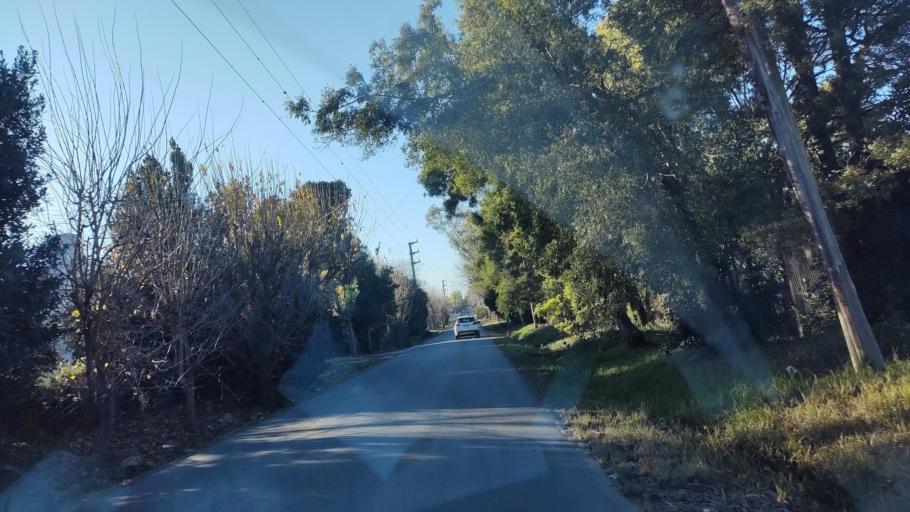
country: AR
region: Buenos Aires
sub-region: Partido de La Plata
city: La Plata
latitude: -34.8839
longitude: -58.0740
